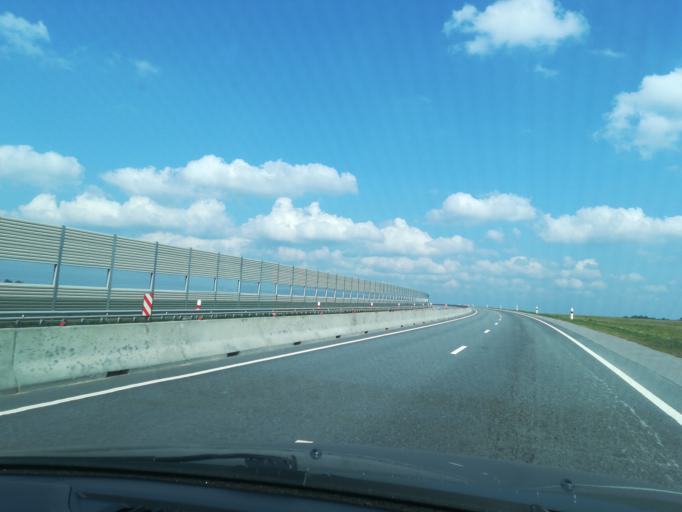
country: RU
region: Leningrad
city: Kingisepp
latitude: 59.5764
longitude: 28.7694
